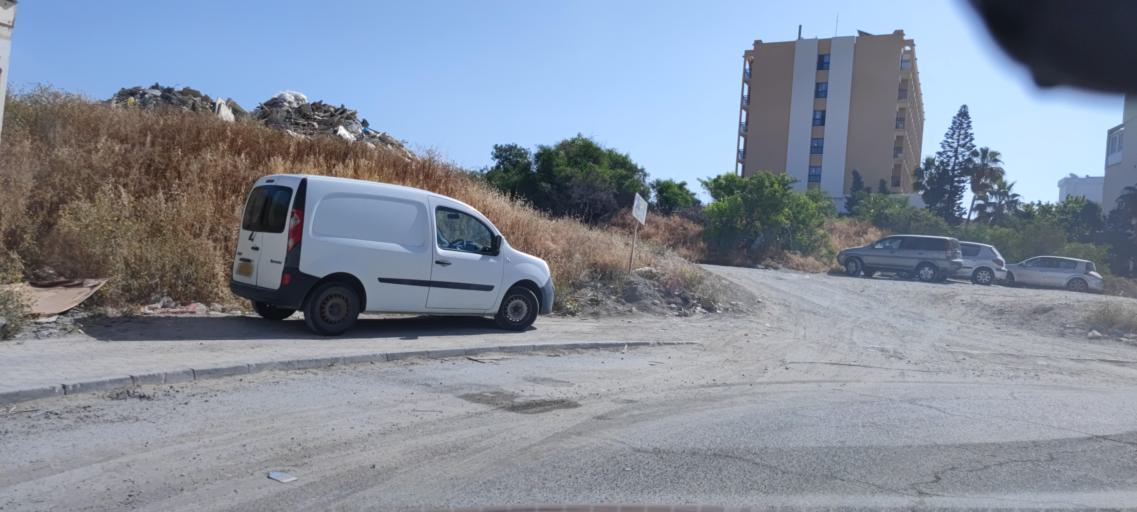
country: CY
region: Limassol
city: Mouttagiaka
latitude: 34.7075
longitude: 33.1176
